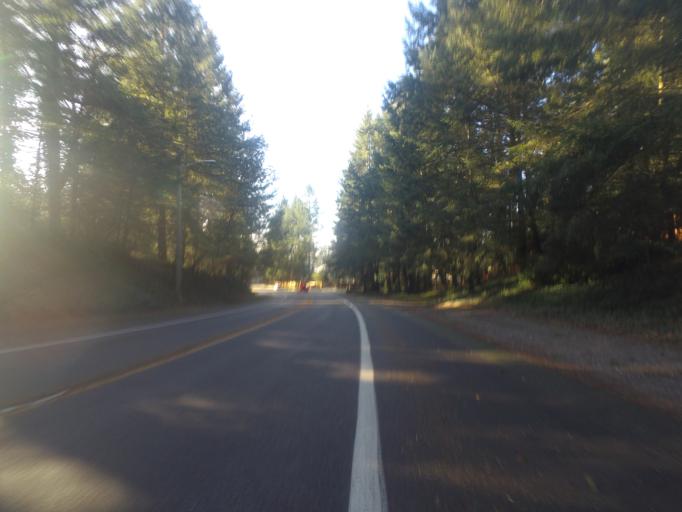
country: US
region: Washington
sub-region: Pierce County
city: University Place
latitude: 47.2117
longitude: -122.5646
